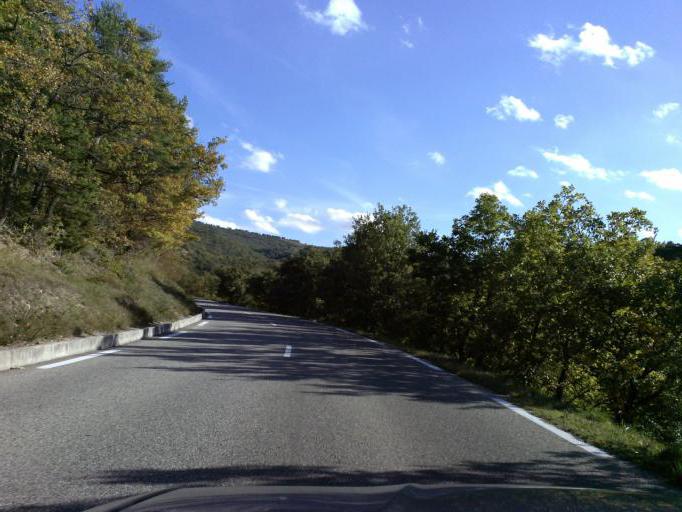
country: FR
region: Provence-Alpes-Cote d'Azur
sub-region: Departement des Alpes-de-Haute-Provence
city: Riez
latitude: 43.9153
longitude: 6.1347
